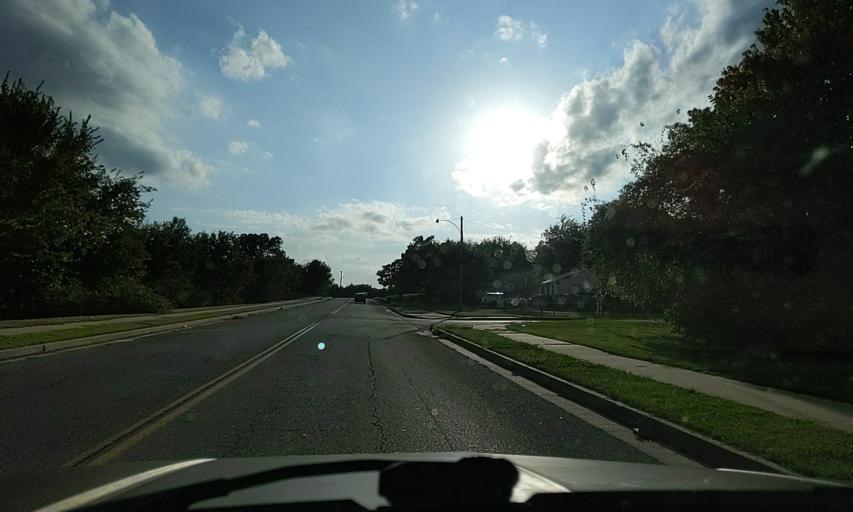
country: US
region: Oklahoma
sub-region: Tulsa County
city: Tulsa
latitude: 36.1946
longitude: -95.9817
